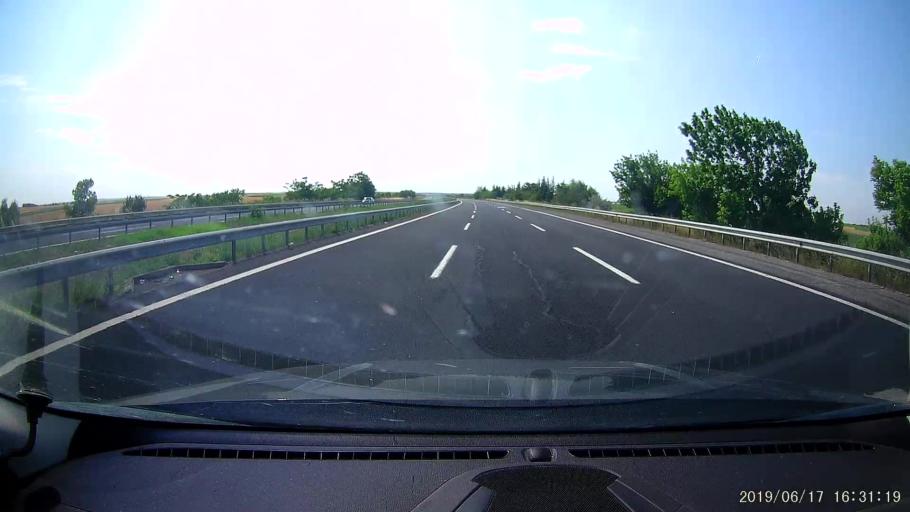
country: TR
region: Tekirdag
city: Beyazkoy
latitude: 41.3608
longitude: 27.6315
